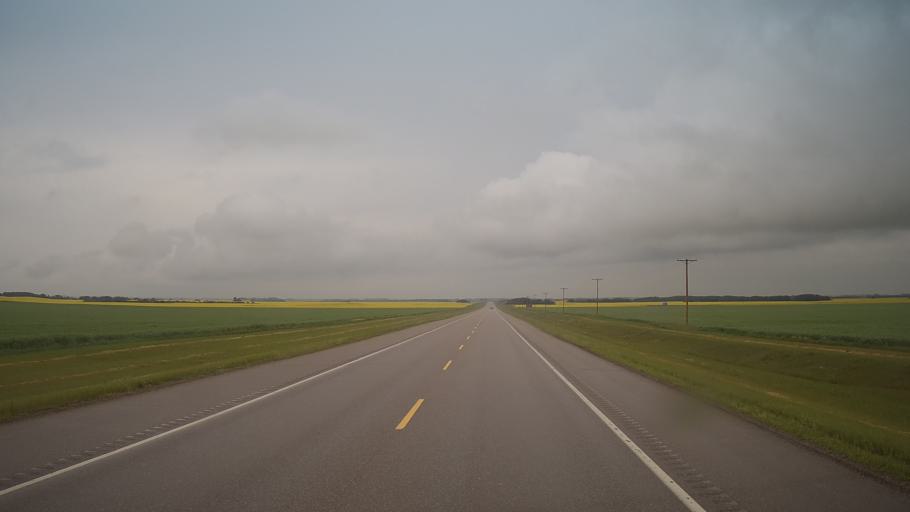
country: CA
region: Saskatchewan
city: Wilkie
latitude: 52.4208
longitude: -108.8961
